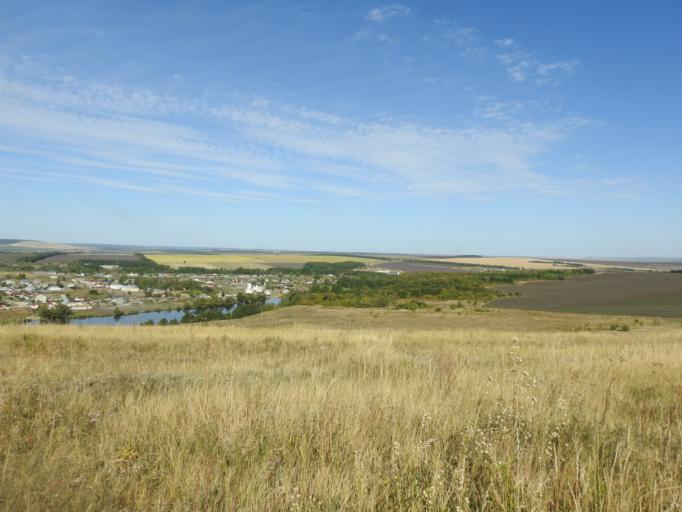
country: RU
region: Saratov
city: Novyye Burasy
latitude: 52.1398
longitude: 46.2461
